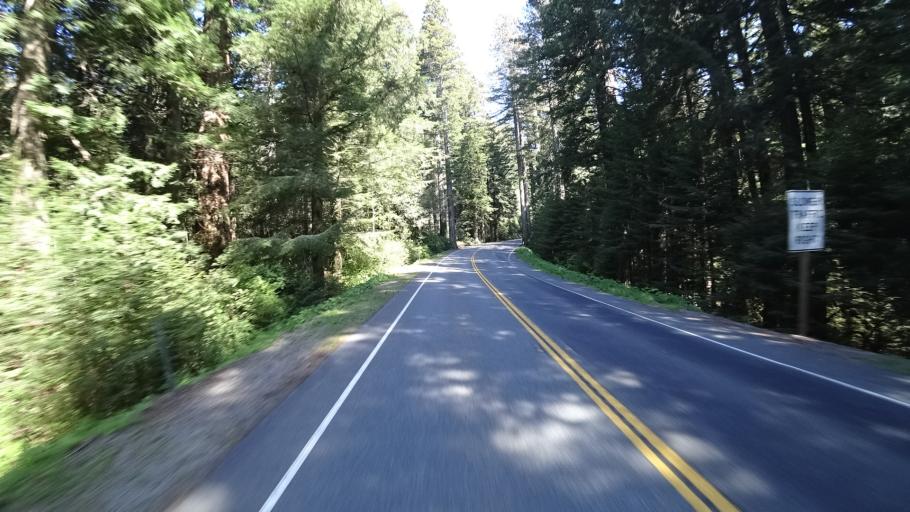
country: US
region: California
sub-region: Del Norte County
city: Bertsch-Oceanview
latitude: 41.6802
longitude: -124.1139
